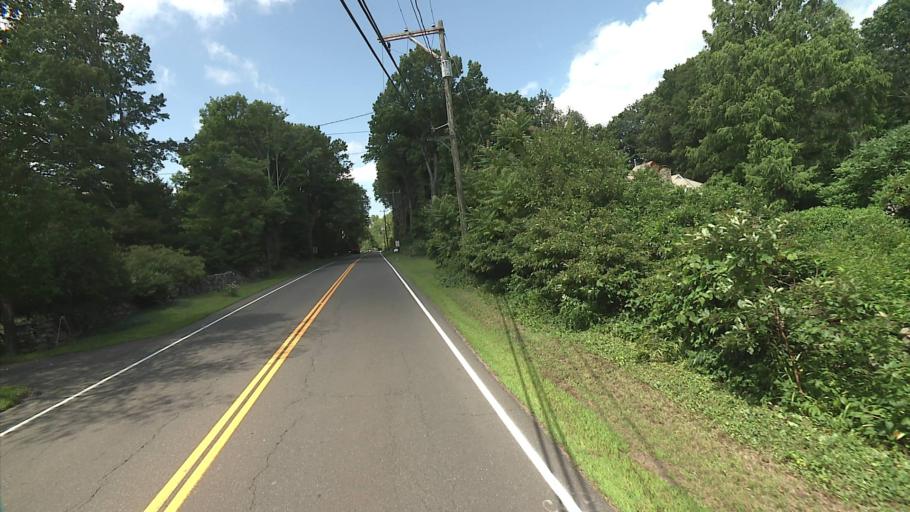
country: US
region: Connecticut
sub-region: Middlesex County
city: Higganum
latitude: 41.3988
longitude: -72.5621
